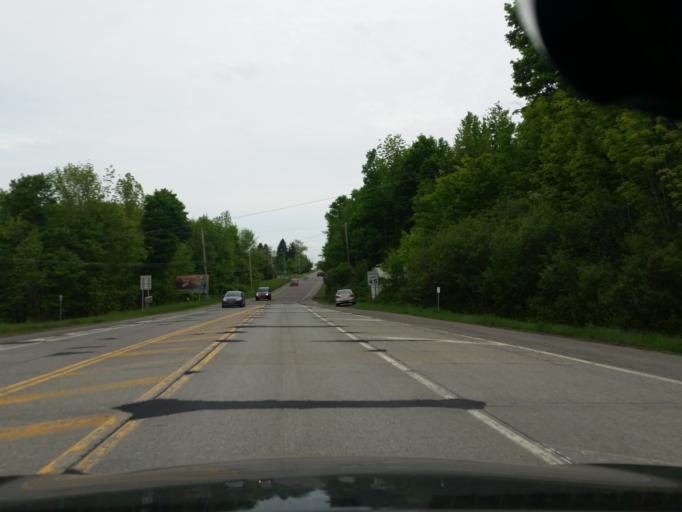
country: US
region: New York
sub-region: Chautauqua County
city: Lakewood
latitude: 42.1450
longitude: -79.4029
